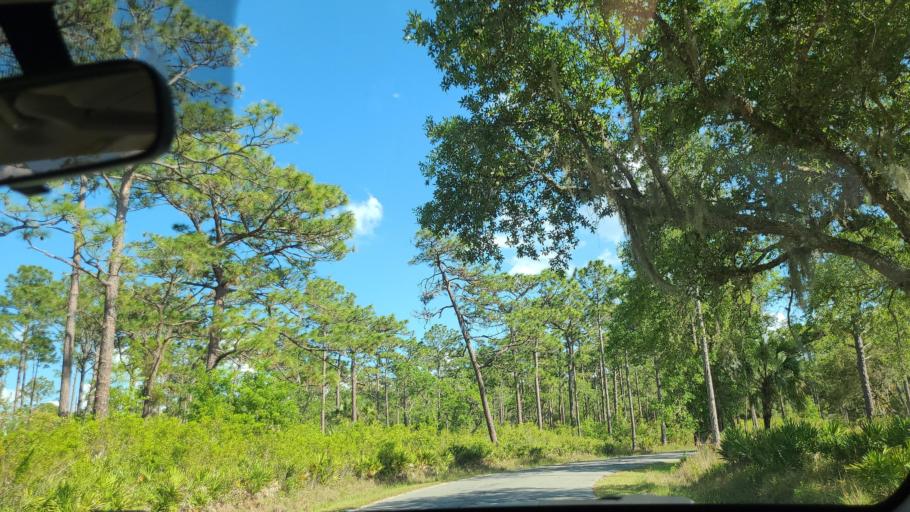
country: US
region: Florida
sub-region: Polk County
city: Babson Park
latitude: 27.9543
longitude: -81.3740
